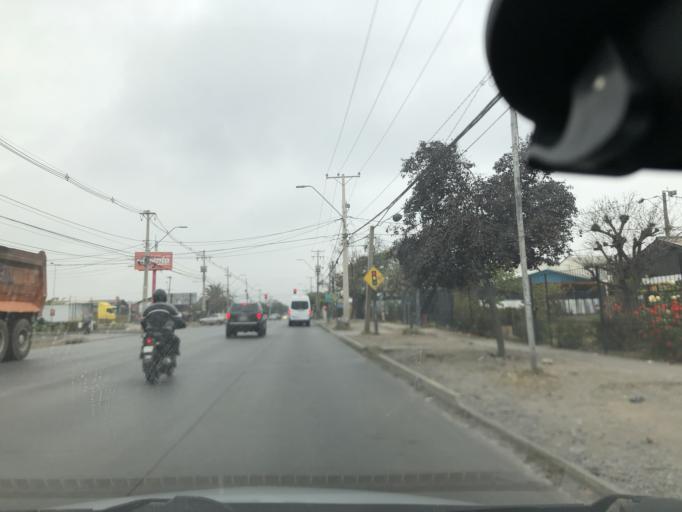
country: CL
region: Santiago Metropolitan
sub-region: Provincia de Santiago
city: La Pintana
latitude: -33.5826
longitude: -70.6066
